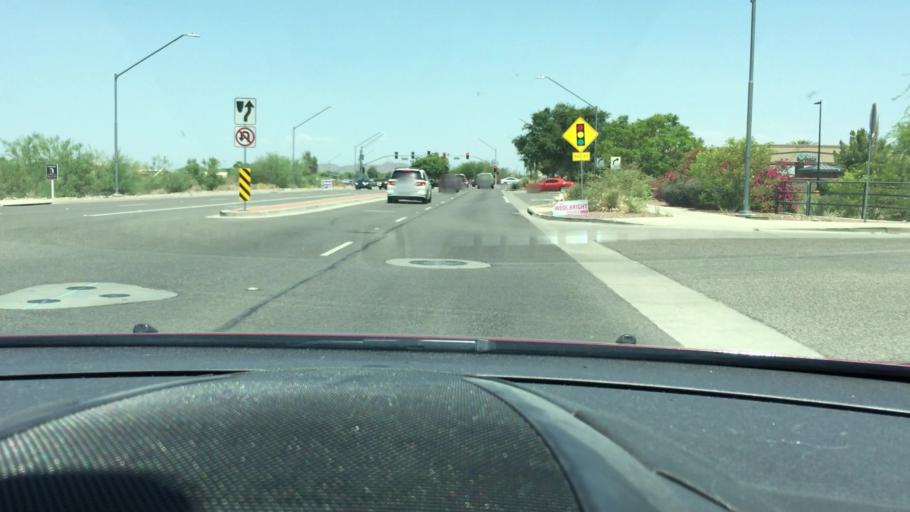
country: US
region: Arizona
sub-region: Maricopa County
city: Sun City
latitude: 33.6476
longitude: -112.2368
